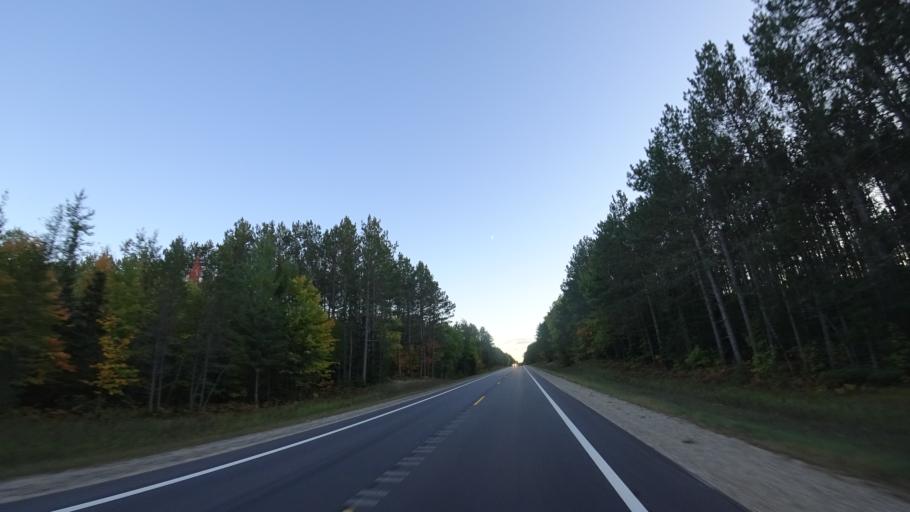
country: US
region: Michigan
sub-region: Luce County
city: Newberry
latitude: 46.3216
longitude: -85.0093
